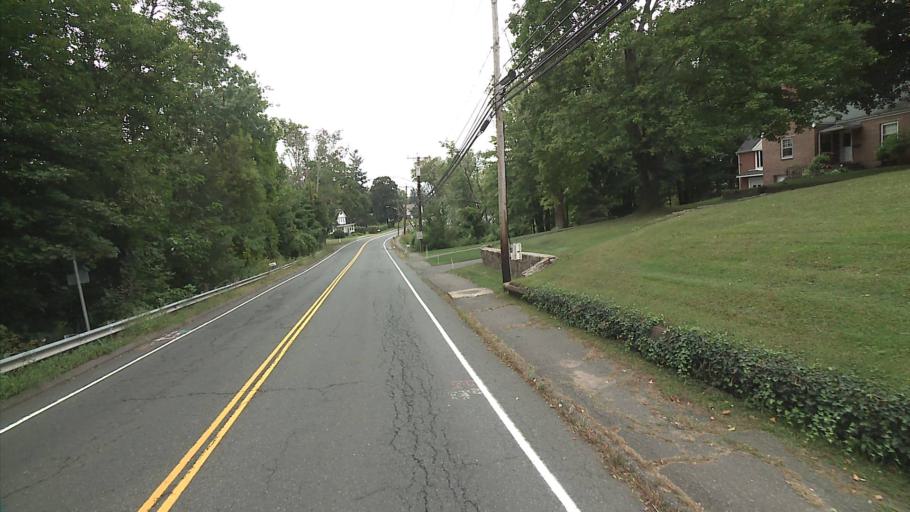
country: US
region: Connecticut
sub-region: Hartford County
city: Windsor Locks
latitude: 41.9220
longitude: -72.6171
